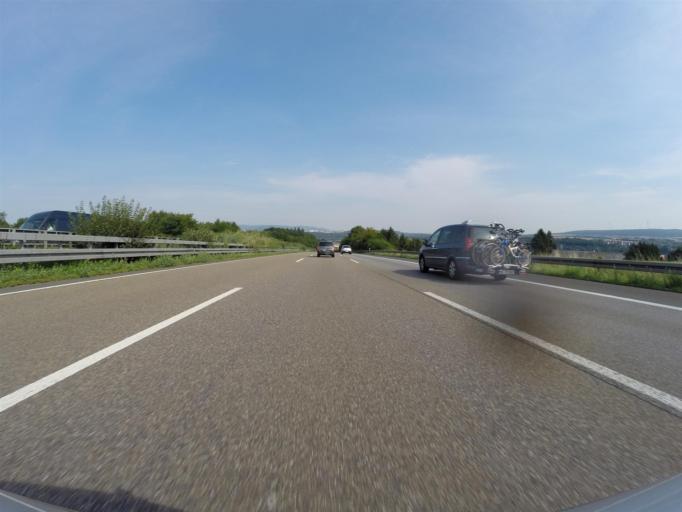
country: DE
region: Hesse
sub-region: Regierungsbezirk Kassel
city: Guxhagen
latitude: 51.2095
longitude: 9.4708
